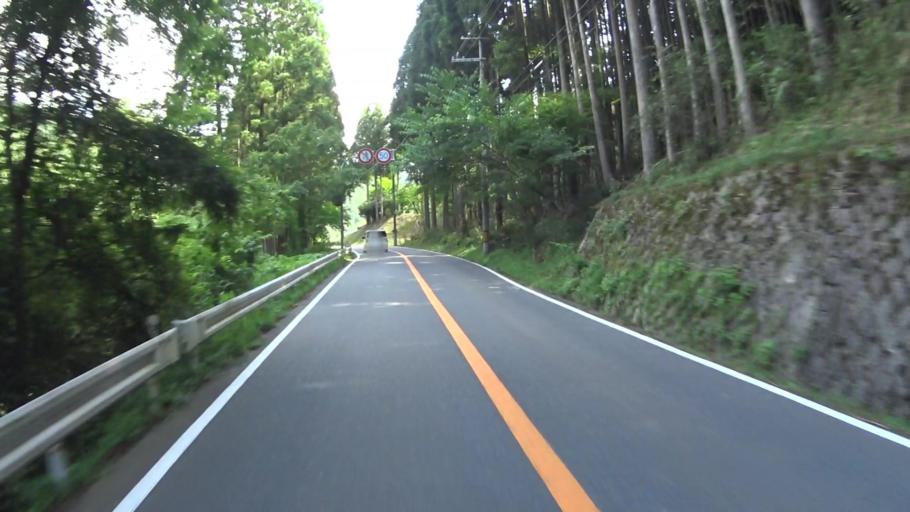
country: JP
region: Kyoto
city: Maizuru
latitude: 35.2855
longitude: 135.5524
